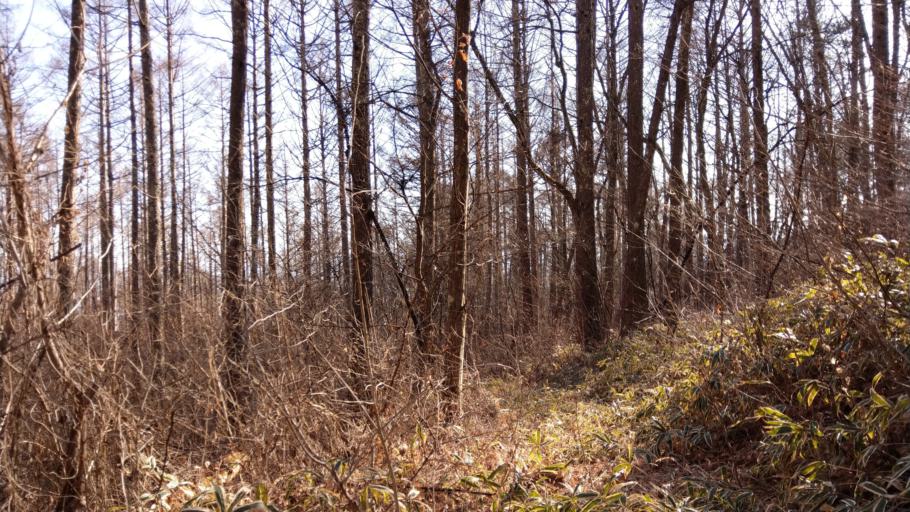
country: JP
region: Nagano
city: Komoro
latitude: 36.3680
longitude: 138.4305
